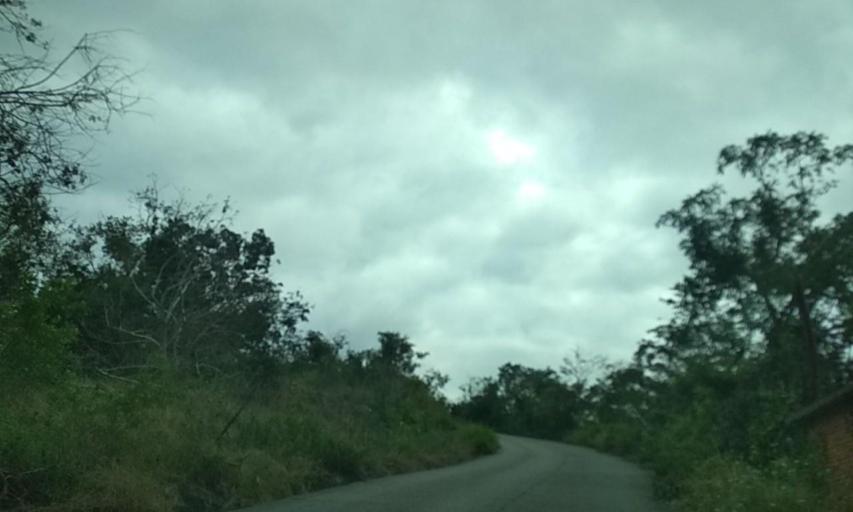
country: MX
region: Veracruz
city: Papantla de Olarte
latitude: 20.4750
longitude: -97.3093
